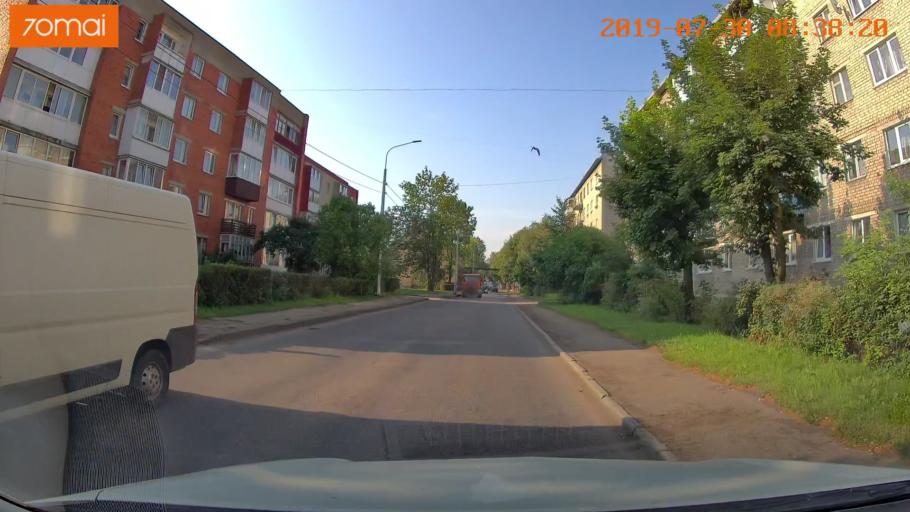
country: RU
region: Kaliningrad
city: Chernyakhovsk
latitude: 54.6354
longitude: 21.8031
